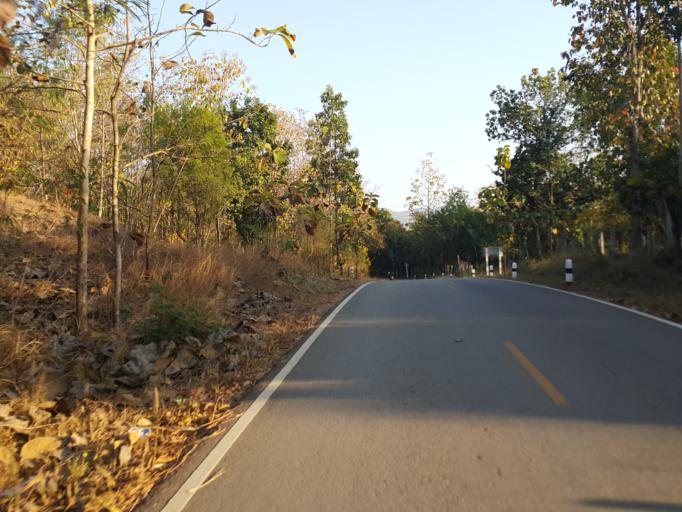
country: TH
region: Chiang Mai
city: Mae On
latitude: 18.7962
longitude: 99.2511
